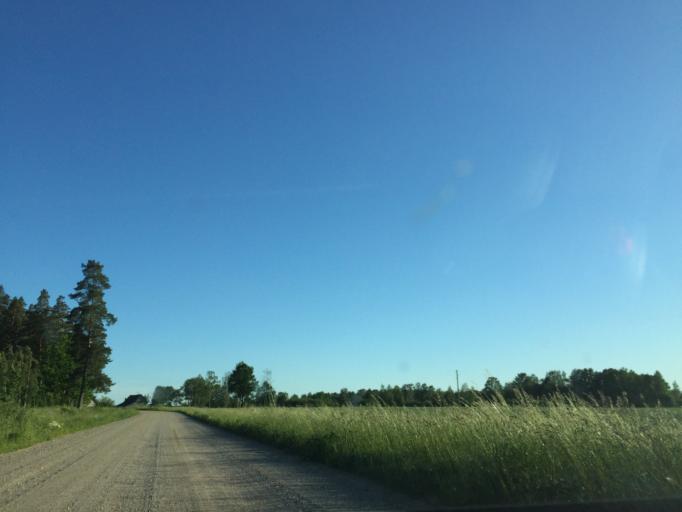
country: LV
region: Talsu Rajons
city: Sabile
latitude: 56.8710
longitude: 22.6062
